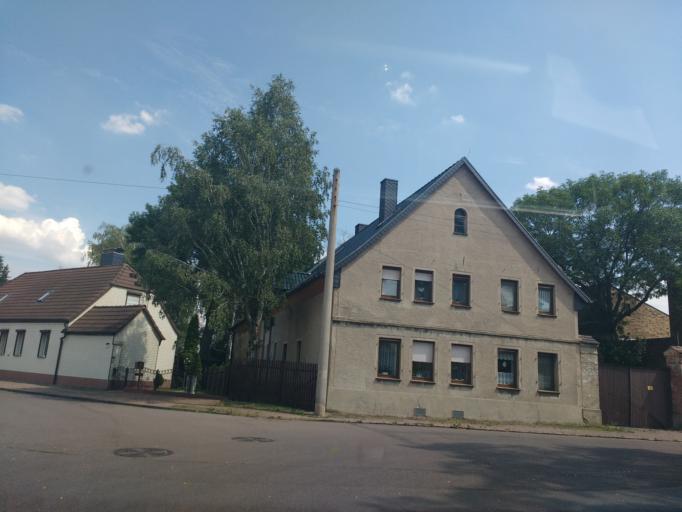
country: DE
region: Saxony-Anhalt
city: Dolbau
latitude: 51.4573
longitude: 12.0393
